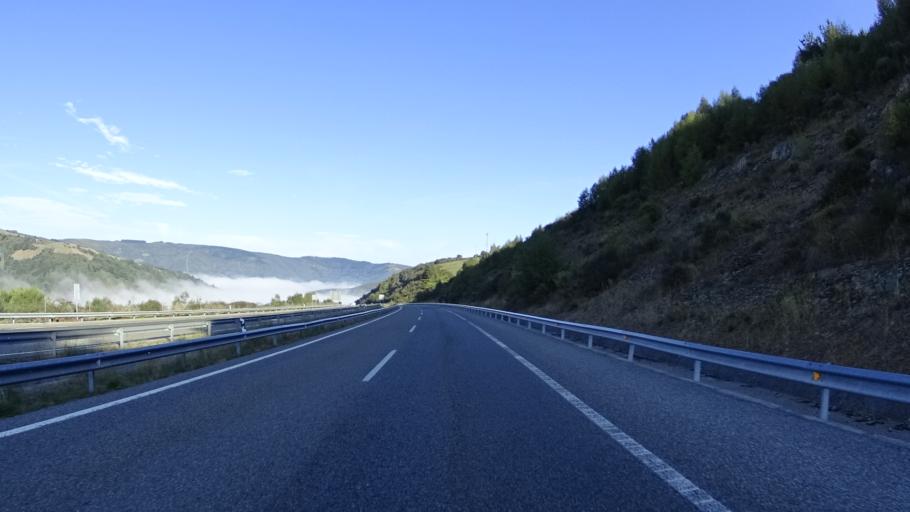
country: ES
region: Galicia
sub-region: Provincia de Lugo
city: San Roman
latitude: 42.7690
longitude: -7.0883
